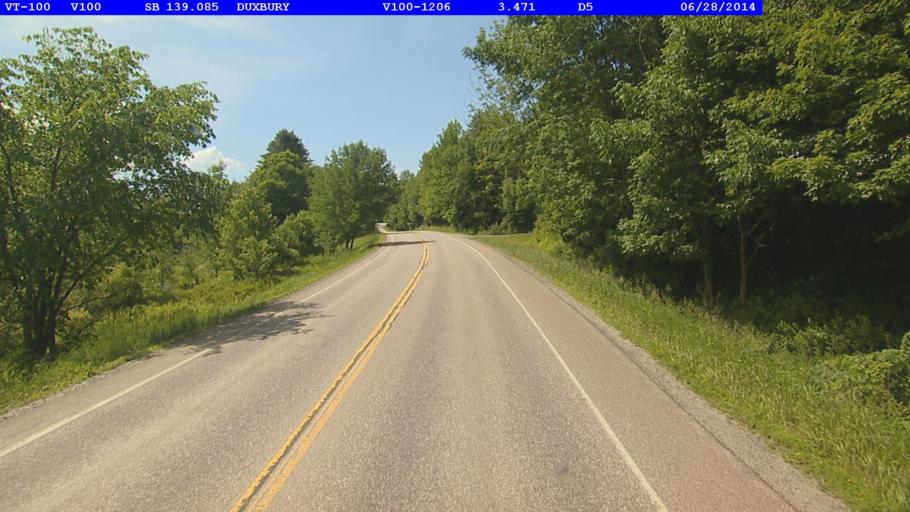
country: US
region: Vermont
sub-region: Washington County
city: Waterbury
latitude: 44.2944
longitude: -72.7752
